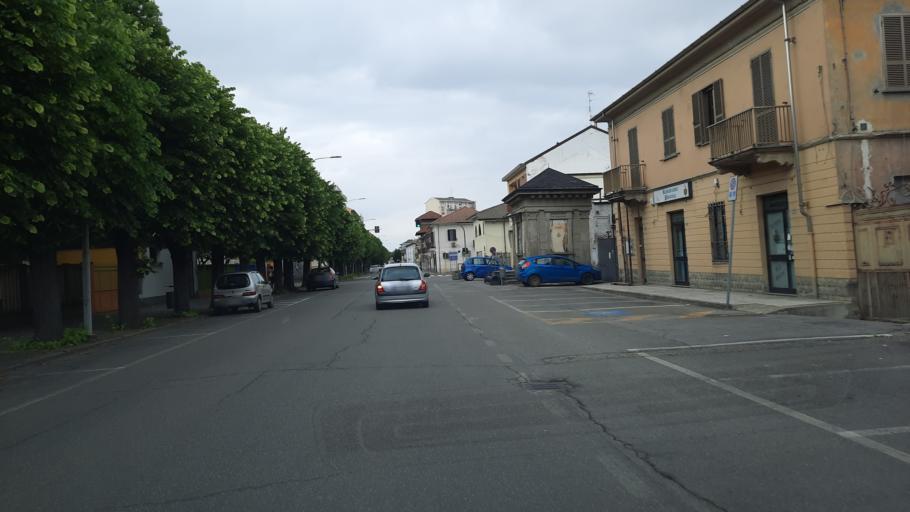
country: IT
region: Lombardy
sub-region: Provincia di Pavia
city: Robbio
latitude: 45.2882
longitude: 8.5959
